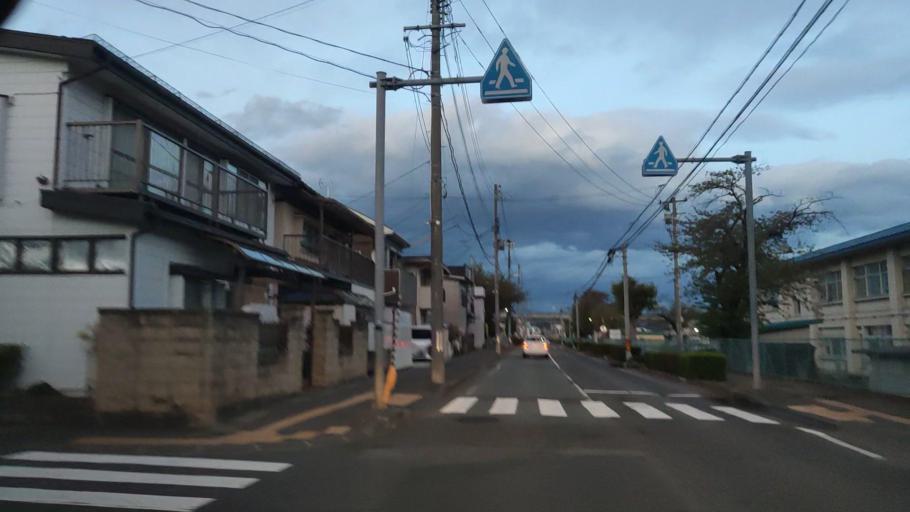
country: JP
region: Iwate
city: Morioka-shi
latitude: 39.7234
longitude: 141.1125
